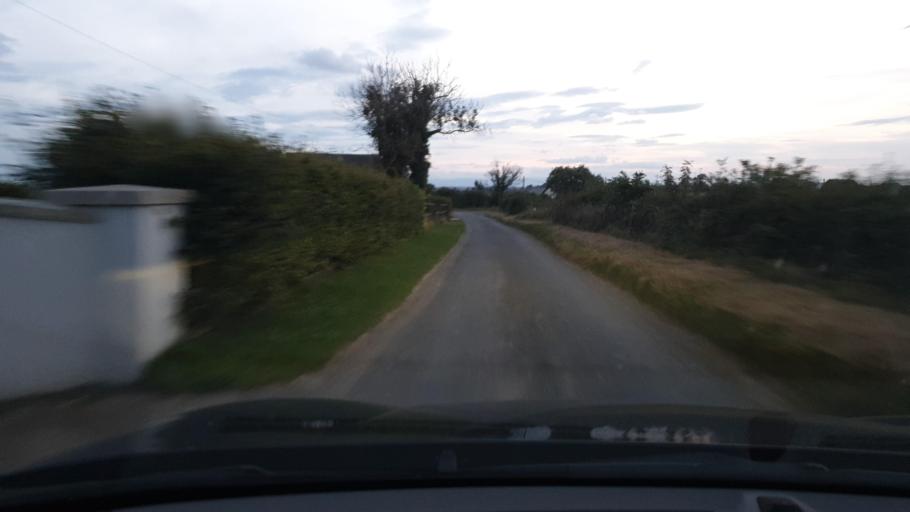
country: IE
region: Leinster
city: An Ros
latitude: 53.5353
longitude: -6.1259
